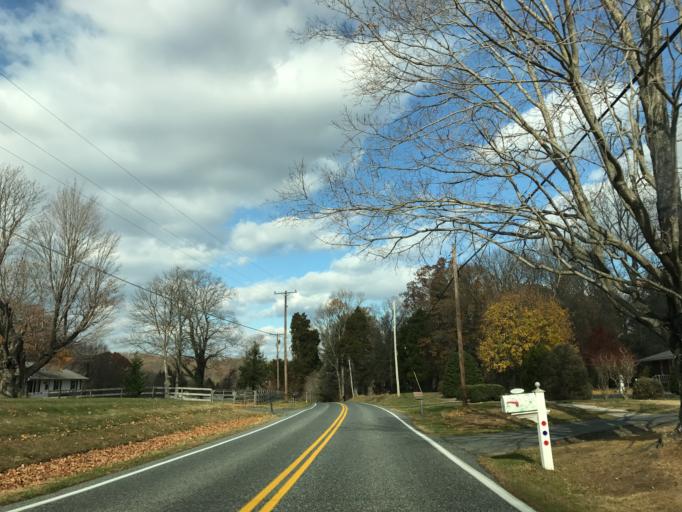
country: US
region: Maryland
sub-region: Harford County
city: Pleasant Hills
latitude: 39.4866
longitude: -76.3743
